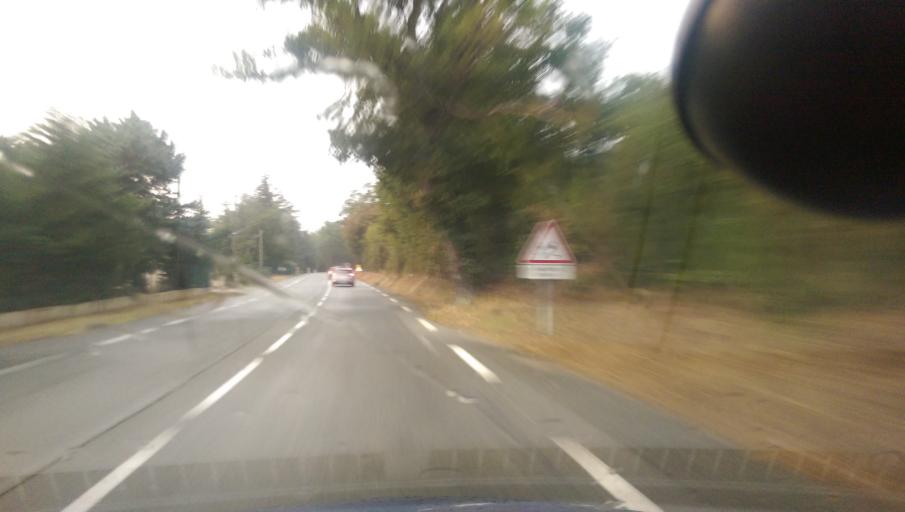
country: FR
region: Provence-Alpes-Cote d'Azur
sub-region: Departement des Alpes-Maritimes
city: Saint-Vallier-de-Thiey
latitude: 43.6869
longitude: 6.8769
